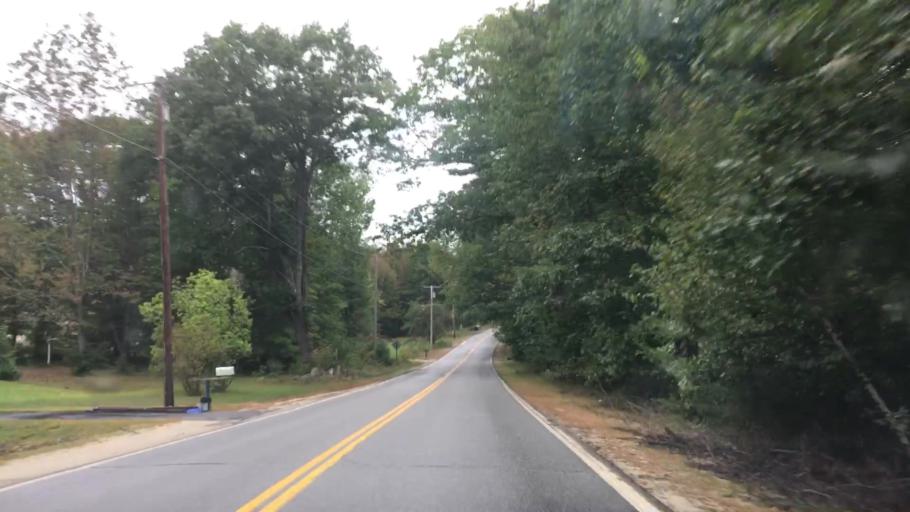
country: US
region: Maine
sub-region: Cumberland County
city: Raymond
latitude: 43.9649
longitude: -70.4658
